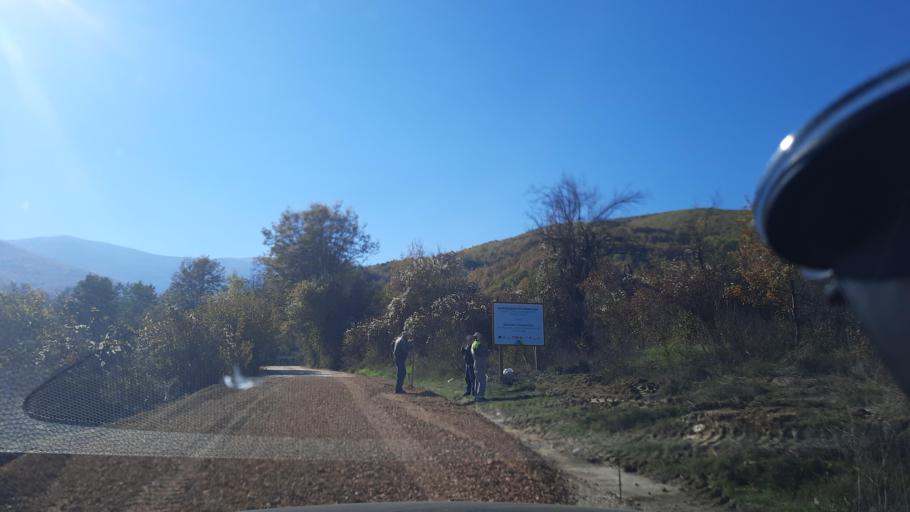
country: MK
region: Demir Hisar
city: Sopotnica
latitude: 41.2743
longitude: 21.0888
